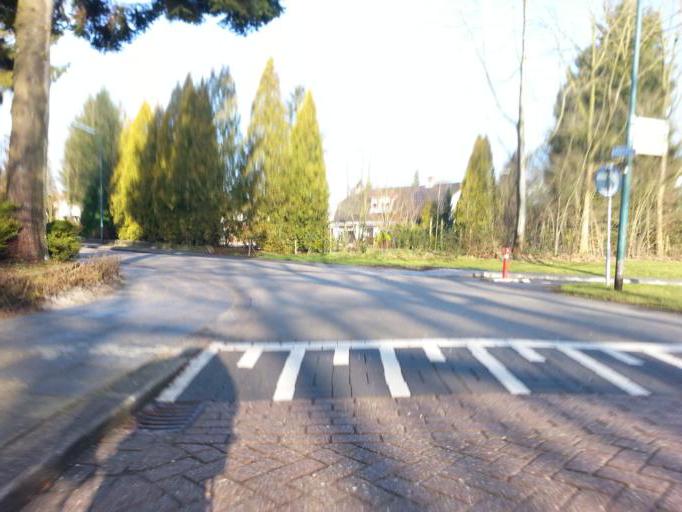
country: NL
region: Utrecht
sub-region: Gemeente Utrechtse Heuvelrug
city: Maarn
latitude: 52.0619
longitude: 5.3749
